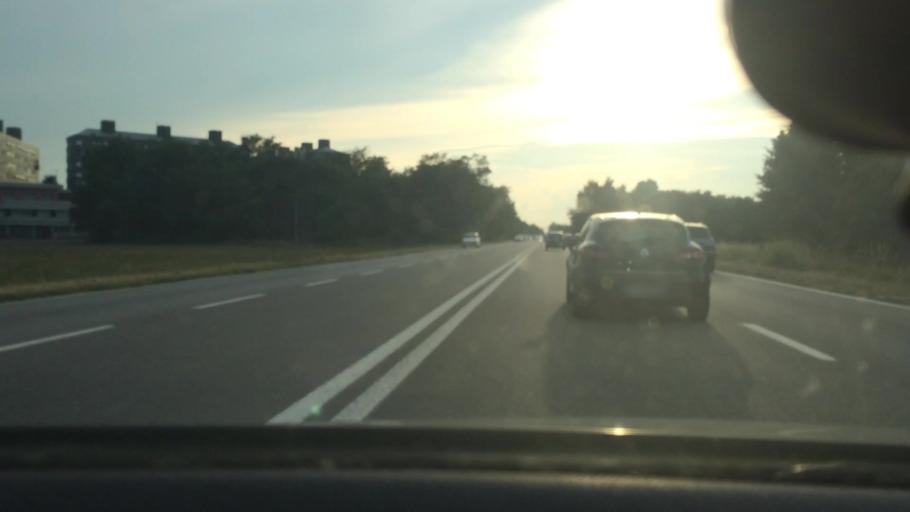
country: IT
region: Lombardy
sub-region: Citta metropolitana di Milano
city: Passirana
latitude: 45.5390
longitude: 9.0410
